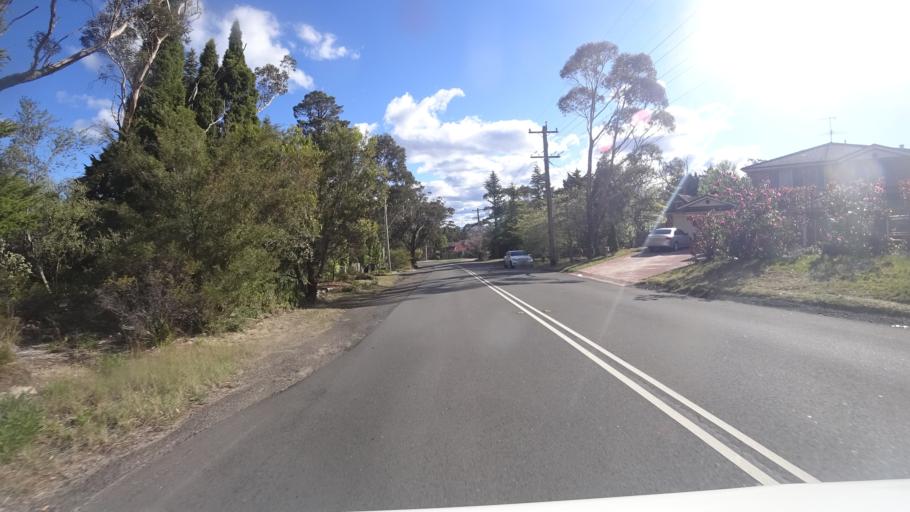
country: AU
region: New South Wales
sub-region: Blue Mountains Municipality
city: Katoomba
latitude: -33.7185
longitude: 150.2945
